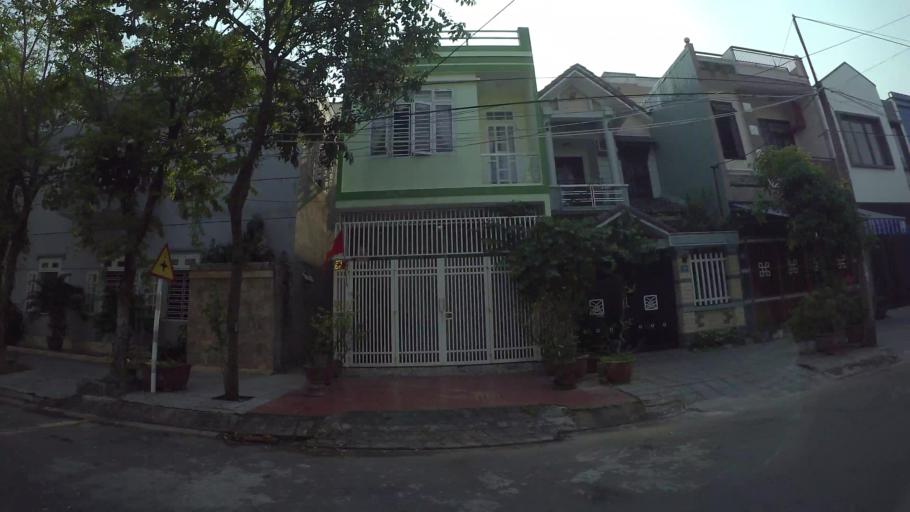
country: VN
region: Da Nang
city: Cam Le
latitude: 16.0216
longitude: 108.2092
